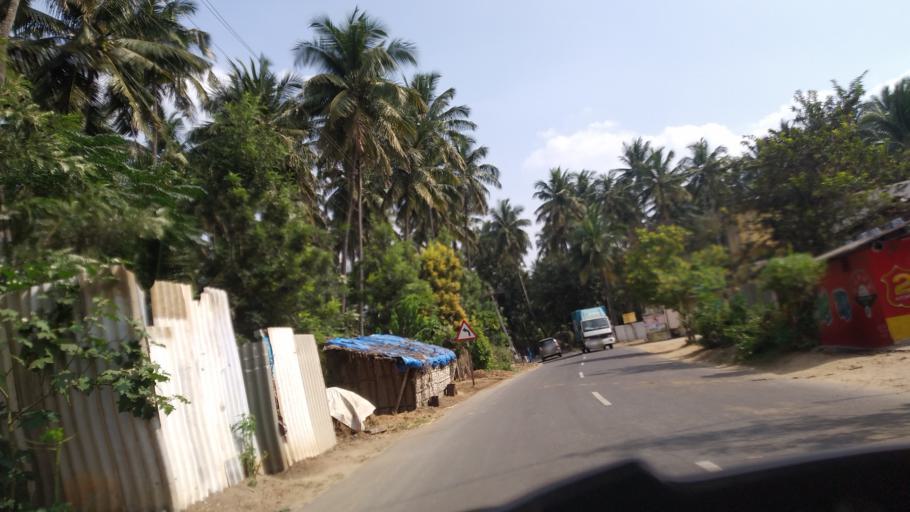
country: IN
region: Tamil Nadu
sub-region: Coimbatore
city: Perur
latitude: 10.9554
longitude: 76.7608
